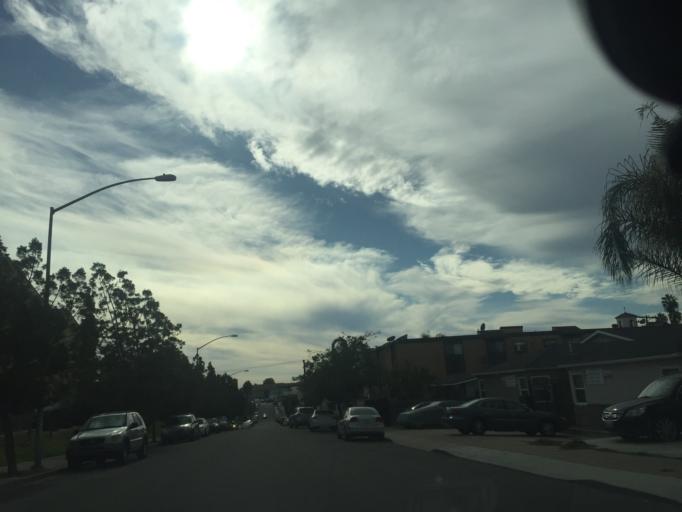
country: US
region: California
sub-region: San Diego County
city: Lemon Grove
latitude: 32.7525
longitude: -117.0901
